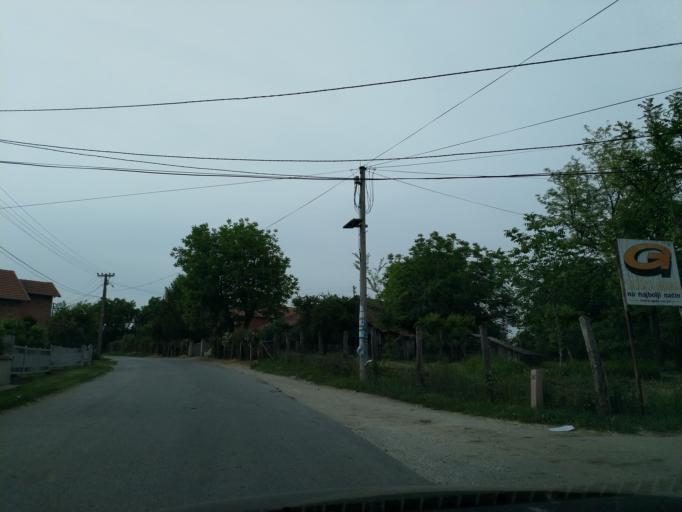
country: RS
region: Central Serbia
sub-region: Pomoravski Okrug
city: Jagodina
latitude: 43.9694
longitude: 21.2274
